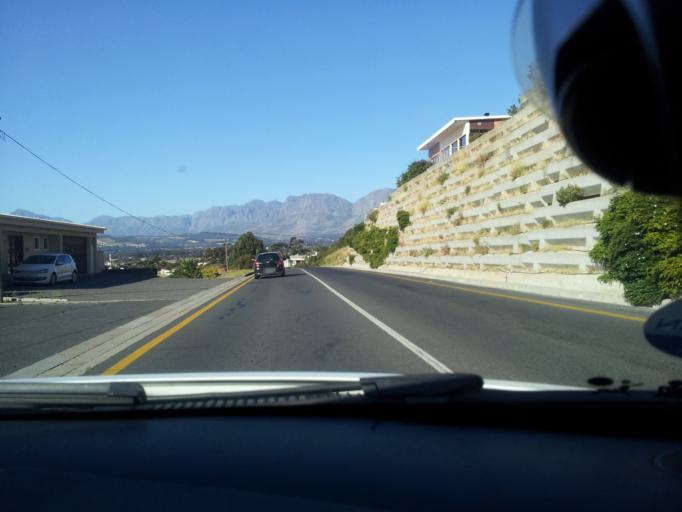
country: ZA
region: Western Cape
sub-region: Overberg District Municipality
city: Grabouw
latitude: -34.1622
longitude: 18.8698
